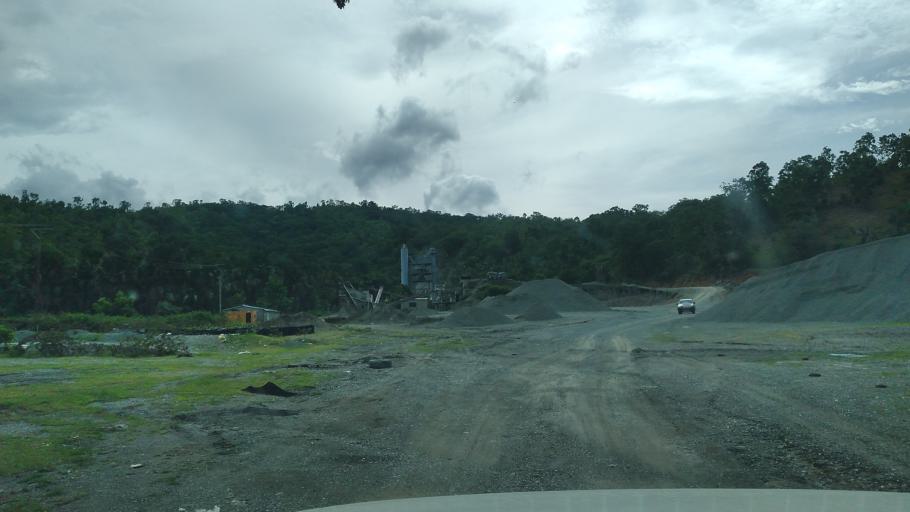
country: TL
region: Dili
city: Dili
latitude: -8.5983
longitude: 125.4793
